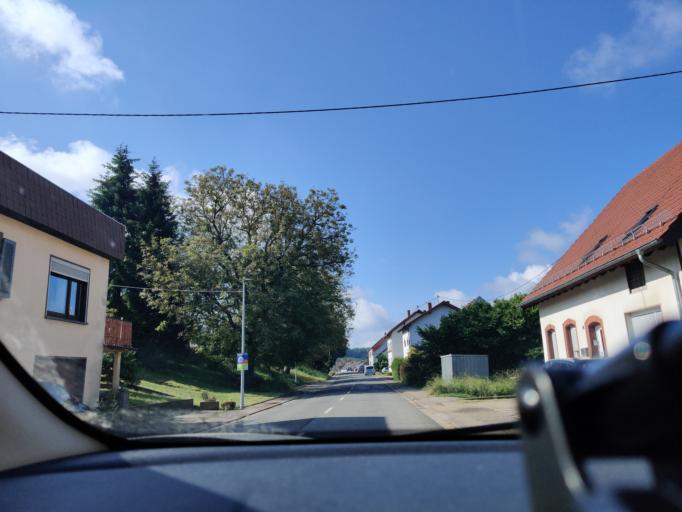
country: DE
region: Saarland
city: Gersheim
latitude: 49.1710
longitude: 7.1614
